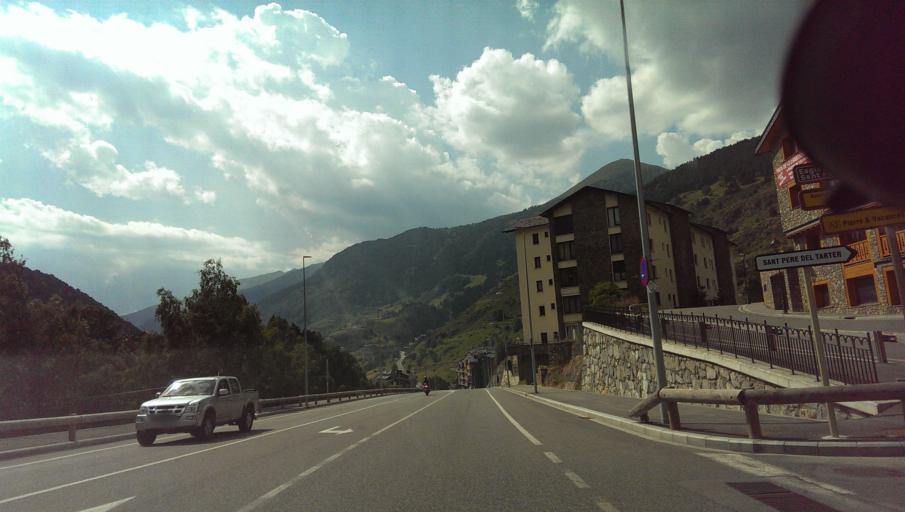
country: AD
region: Canillo
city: El Tarter
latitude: 42.5778
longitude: 1.6539
